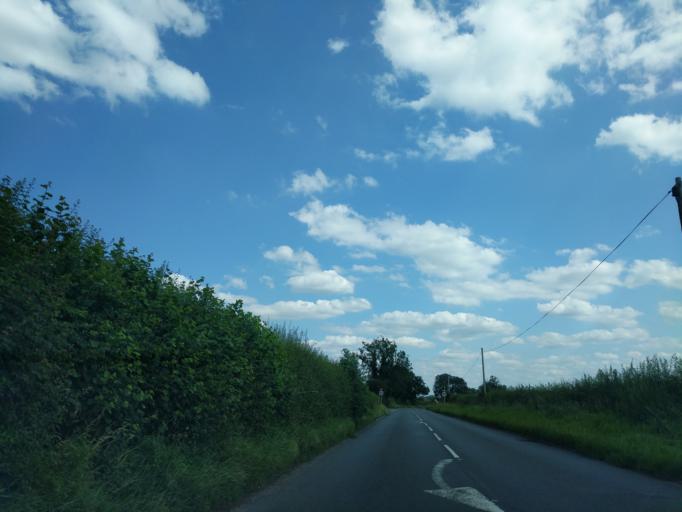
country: GB
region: England
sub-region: Staffordshire
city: Uttoxeter
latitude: 52.9324
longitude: -1.9288
